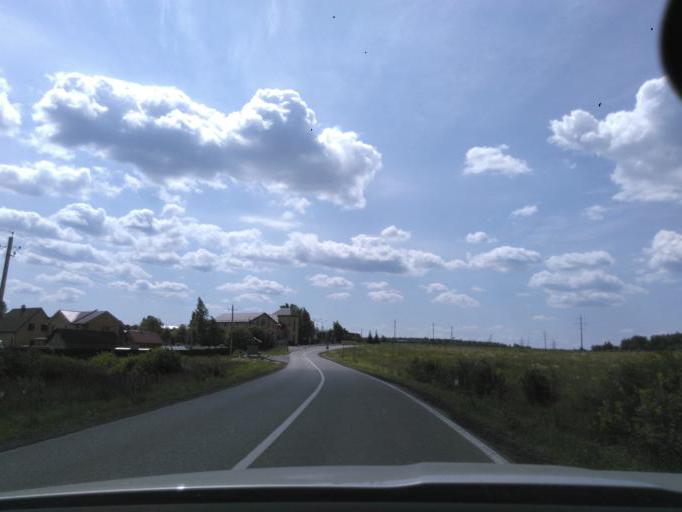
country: RU
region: Moskovskaya
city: Solnechnogorsk
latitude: 56.1503
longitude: 36.9799
